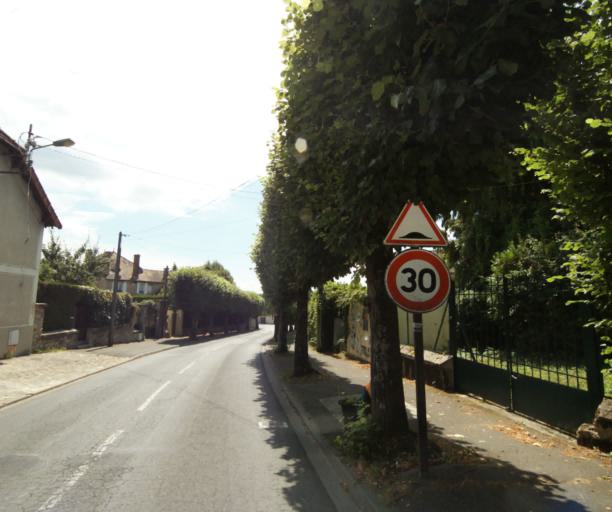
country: FR
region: Ile-de-France
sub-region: Departement de Seine-et-Marne
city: Chartrettes
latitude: 48.4866
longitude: 2.6964
